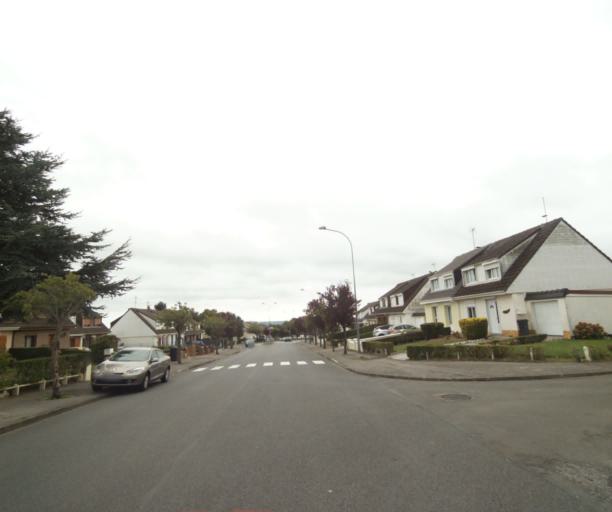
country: FR
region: Nord-Pas-de-Calais
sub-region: Departement du Pas-de-Calais
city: Etaples
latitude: 50.5236
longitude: 1.6389
